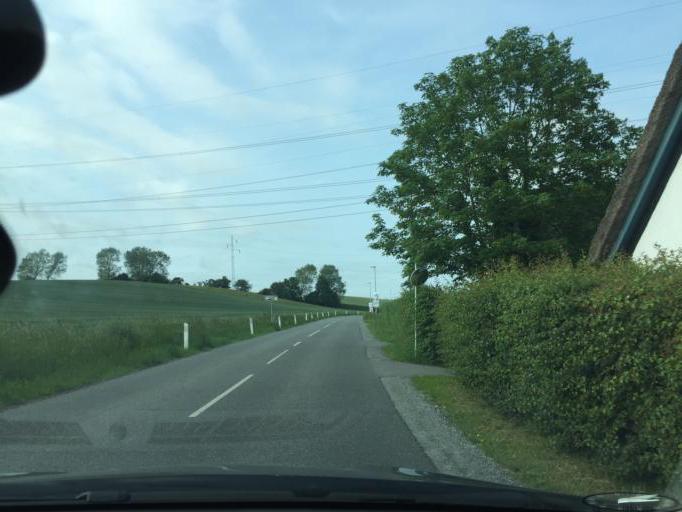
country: DK
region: South Denmark
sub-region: Odense Kommune
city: Bellinge
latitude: 55.3412
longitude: 10.3291
